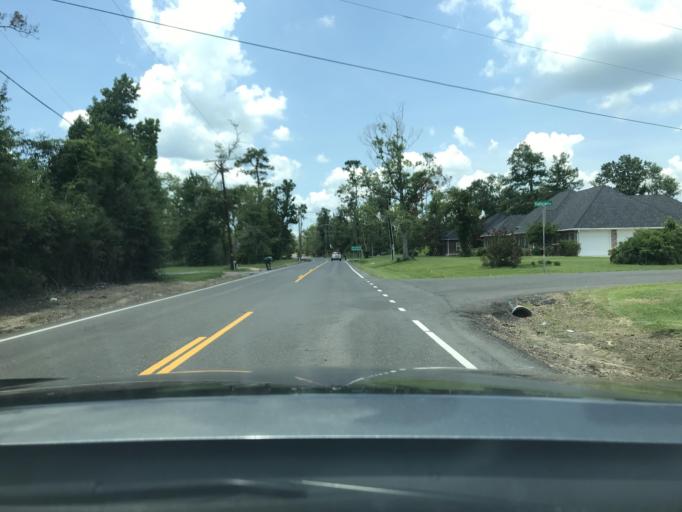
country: US
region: Louisiana
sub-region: Calcasieu Parish
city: Moss Bluff
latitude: 30.3176
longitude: -93.1816
